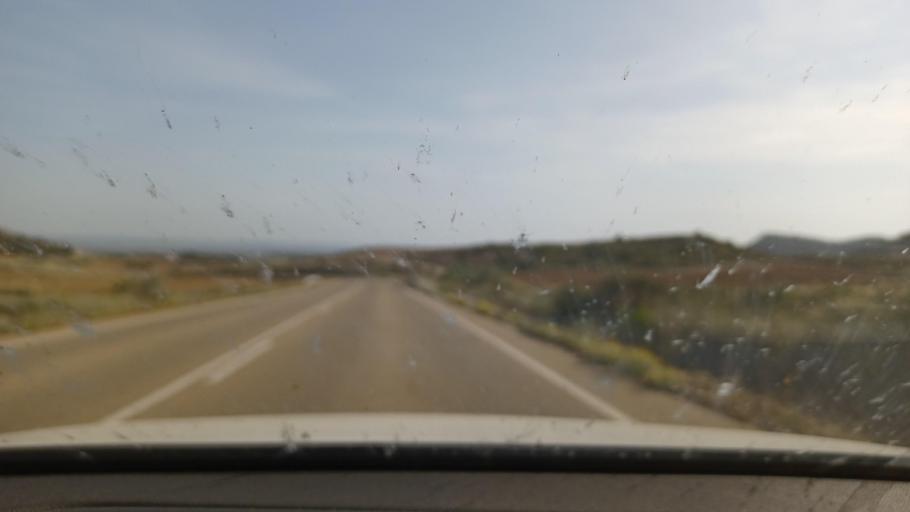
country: ES
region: Aragon
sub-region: Provincia de Zaragoza
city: Chiprana
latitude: 41.3403
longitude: -0.0890
